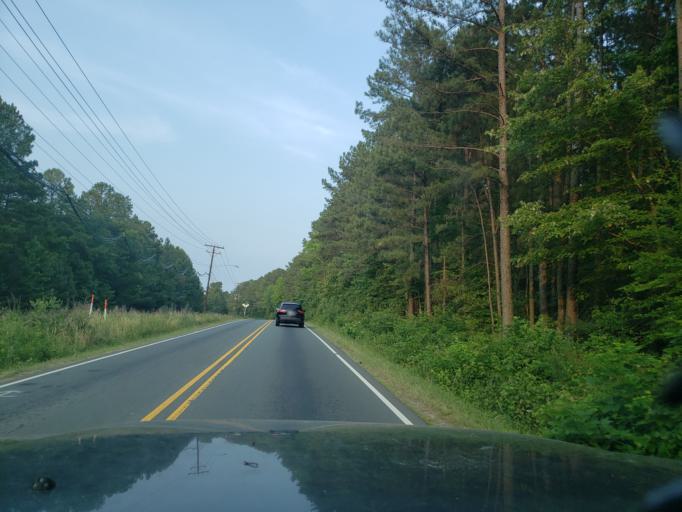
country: US
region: North Carolina
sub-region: Durham County
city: Durham
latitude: 35.9567
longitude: -78.8825
